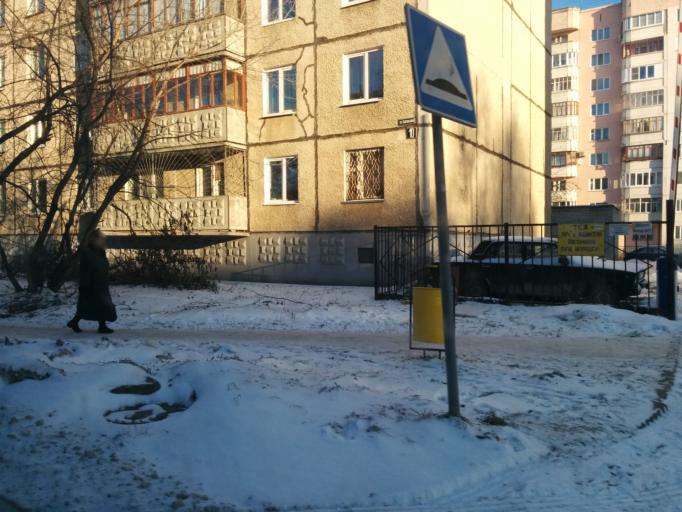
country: RU
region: Perm
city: Kultayevo
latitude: 58.0178
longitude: 55.9782
